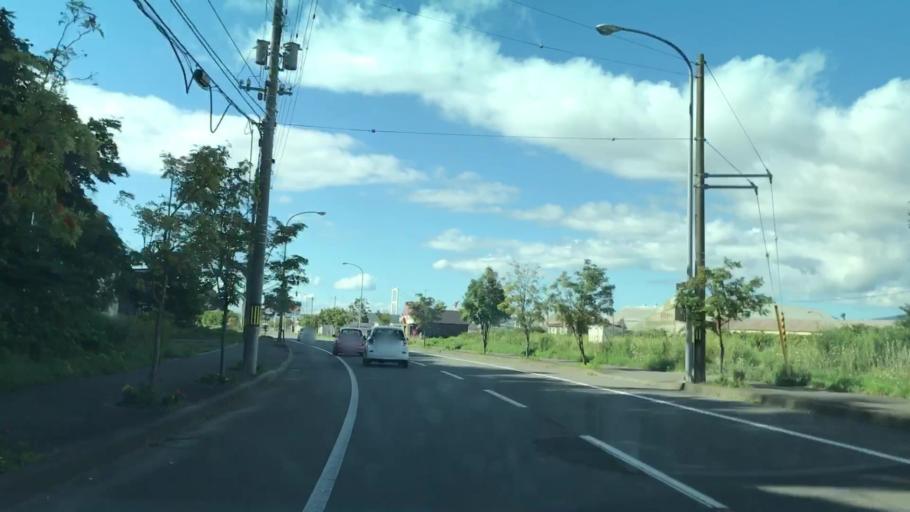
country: JP
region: Hokkaido
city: Muroran
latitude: 42.3294
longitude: 140.9671
